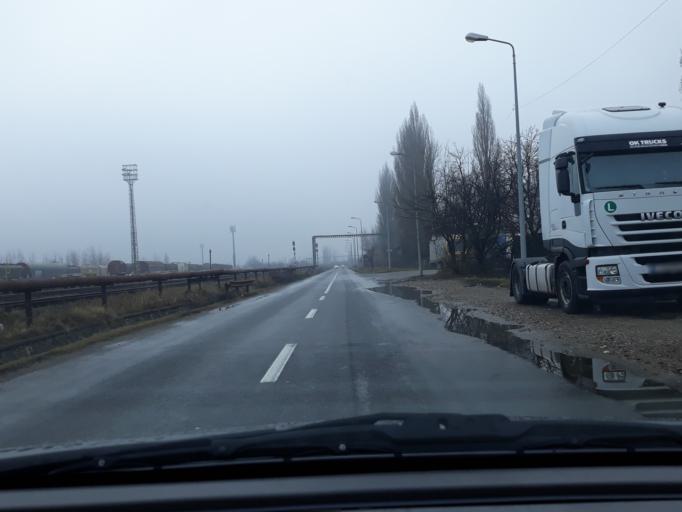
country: RO
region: Bihor
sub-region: Comuna Sanmartin
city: Sanmartin
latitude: 47.0406
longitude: 21.9636
